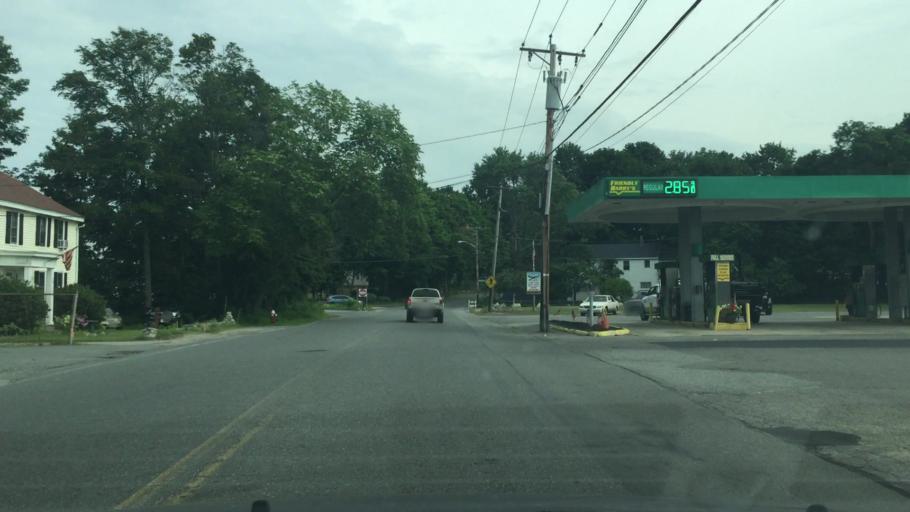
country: US
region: Massachusetts
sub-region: Middlesex County
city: Dracut
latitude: 42.6835
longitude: -71.3547
